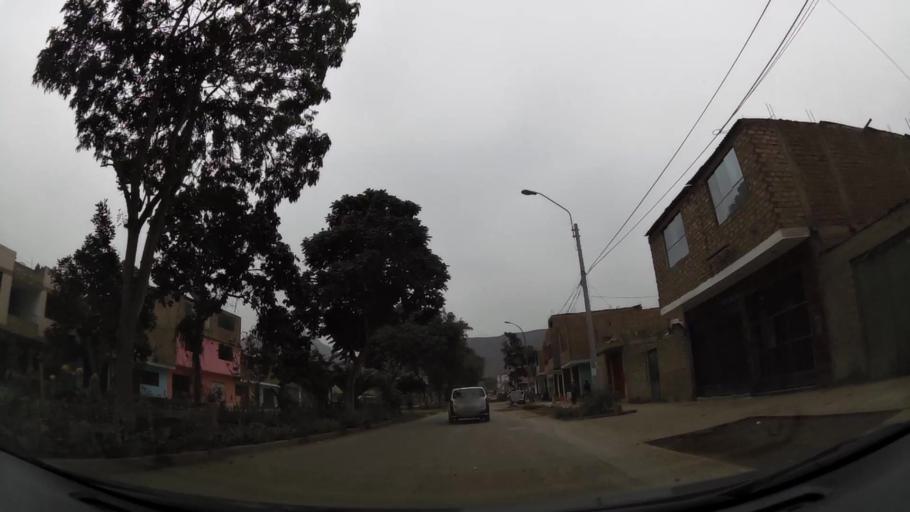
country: PE
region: Lima
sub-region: Lima
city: Urb. Santo Domingo
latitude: -11.9080
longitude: -77.0402
